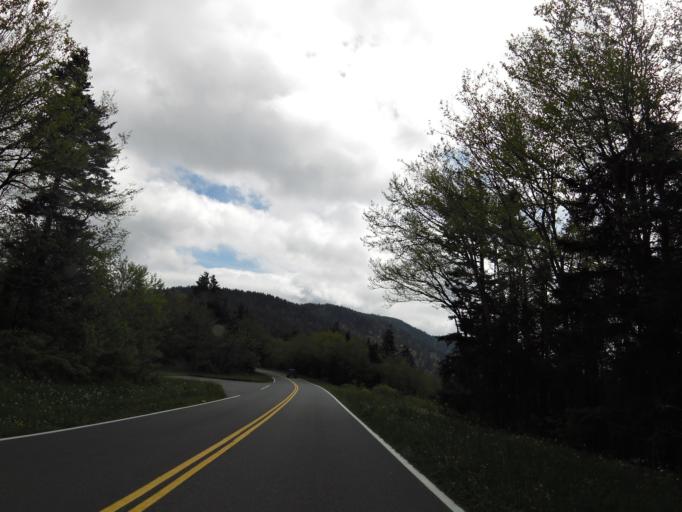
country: US
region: Tennessee
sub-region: Sevier County
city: Gatlinburg
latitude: 35.5784
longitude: -83.4796
